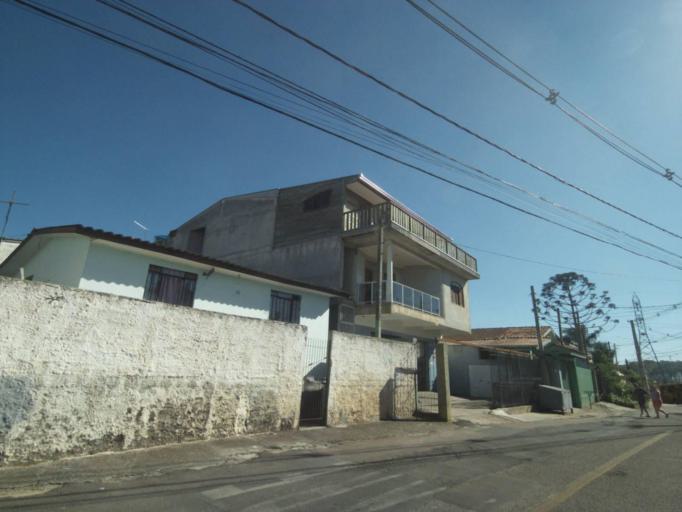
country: BR
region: Parana
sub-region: Curitiba
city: Curitiba
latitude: -25.4608
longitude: -49.3521
